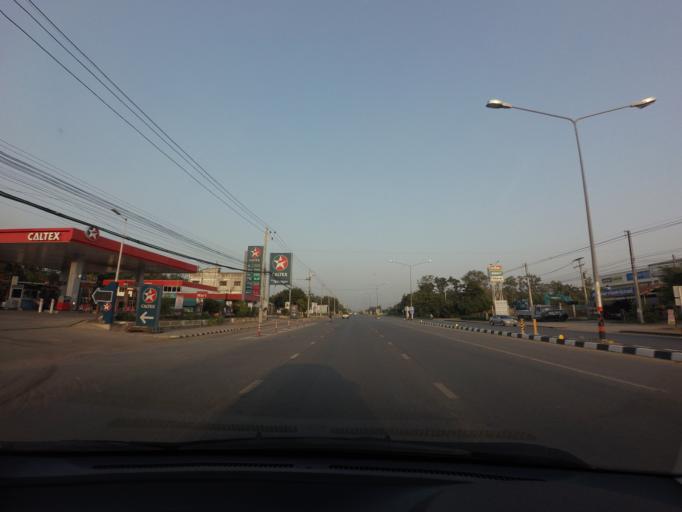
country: TH
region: Sukhothai
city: Sukhothai
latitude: 17.0193
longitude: 99.8595
